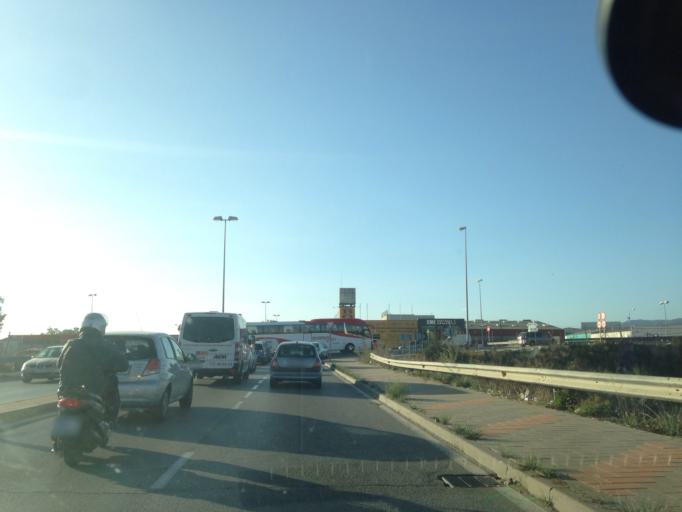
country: ES
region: Andalusia
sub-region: Provincia de Malaga
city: Malaga
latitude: 36.7149
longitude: -4.4831
